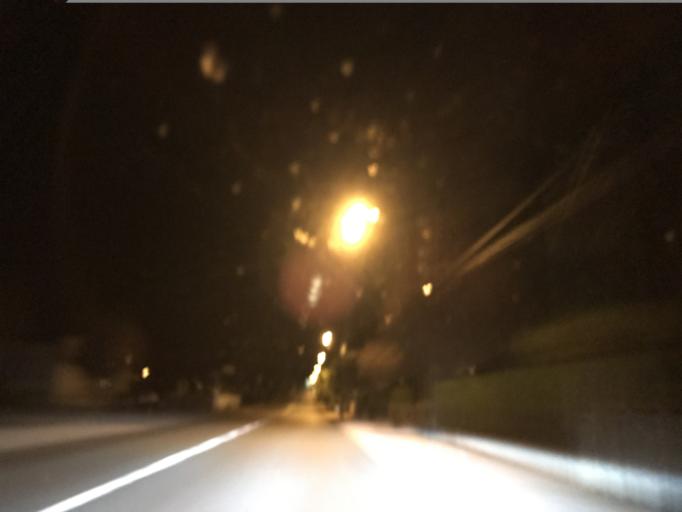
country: FR
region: Auvergne
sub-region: Departement du Puy-de-Dome
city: Puy-Guillaume
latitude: 45.9527
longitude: 3.4789
